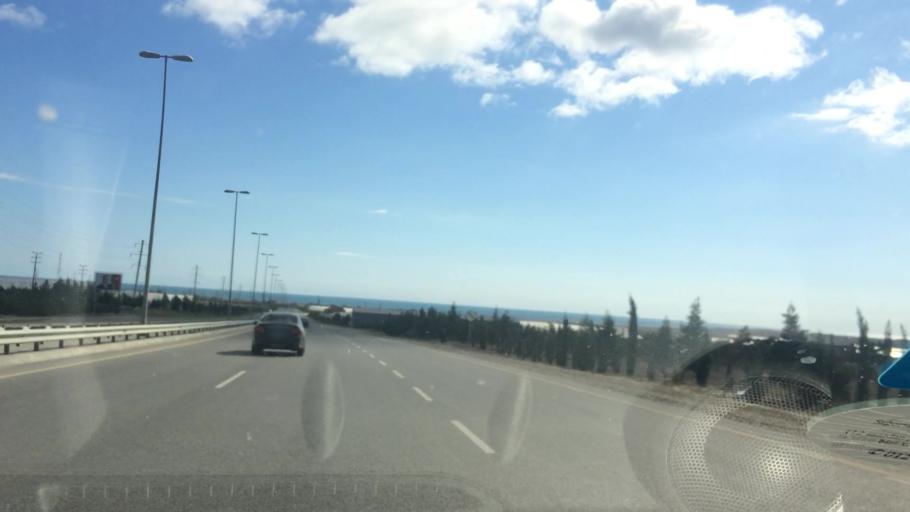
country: AZ
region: Baki
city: Zyrya
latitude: 40.4009
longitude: 50.3115
